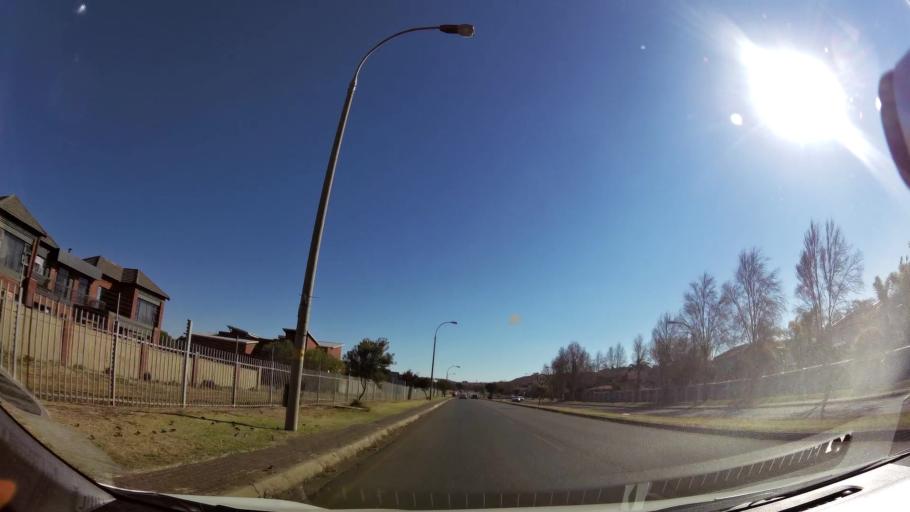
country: ZA
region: Gauteng
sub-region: City of Johannesburg Metropolitan Municipality
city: Johannesburg
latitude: -26.2933
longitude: 28.0913
